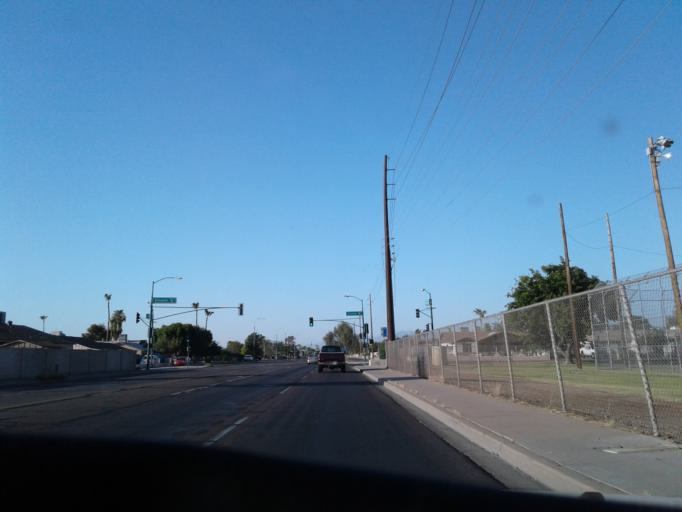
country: US
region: Arizona
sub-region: Maricopa County
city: Glendale
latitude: 33.4739
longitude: -112.1865
